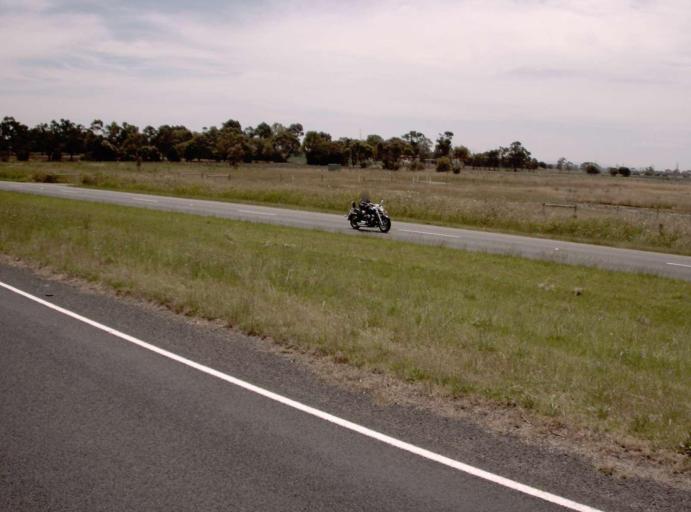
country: AU
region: Victoria
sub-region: Frankston
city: Skye
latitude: -38.0946
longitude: 145.2360
